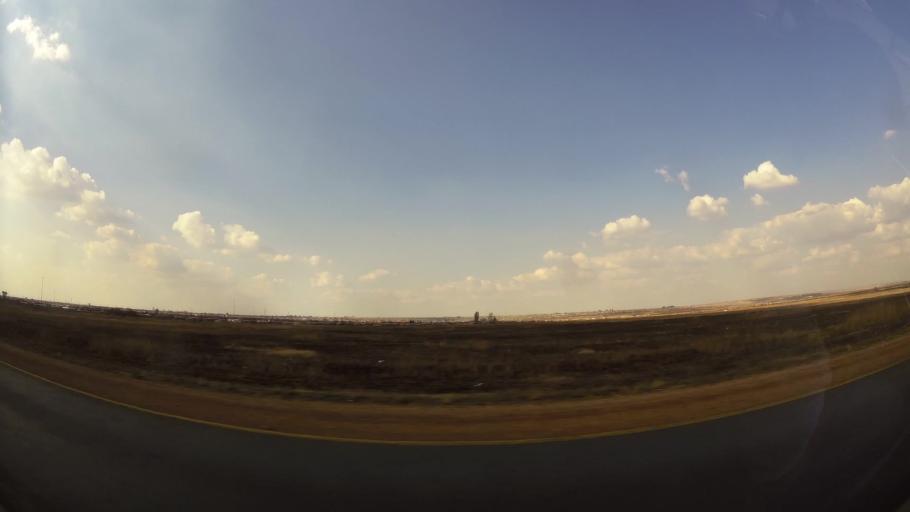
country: ZA
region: Gauteng
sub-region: Sedibeng District Municipality
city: Heidelberg
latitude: -26.3790
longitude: 28.3438
